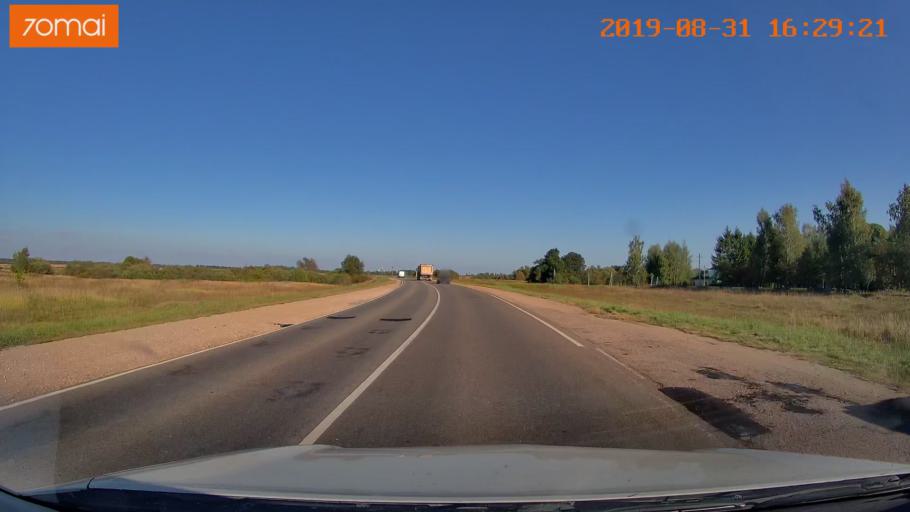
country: RU
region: Kaluga
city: Babynino
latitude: 54.5059
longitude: 35.8030
